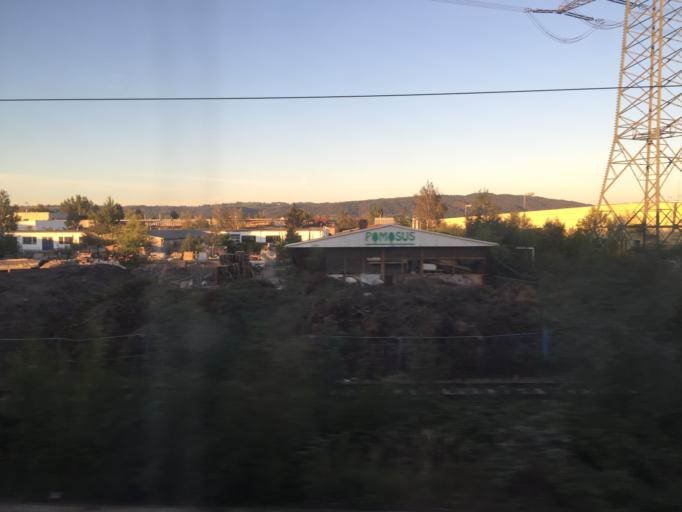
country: DE
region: Saxony
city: Heidenau
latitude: 50.9882
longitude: 13.8473
